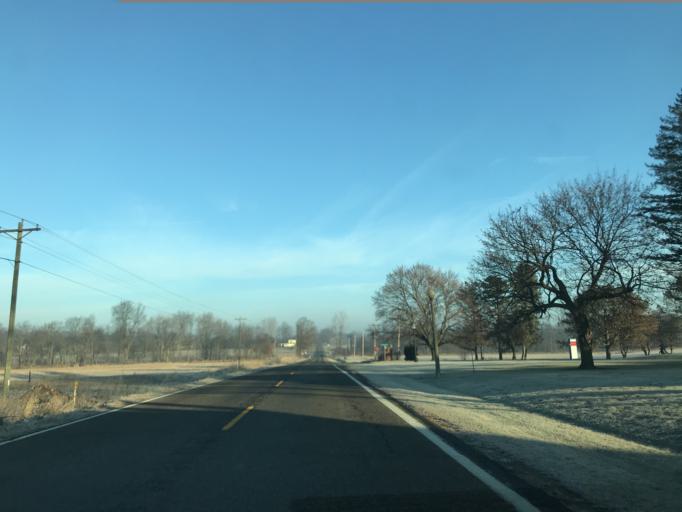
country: US
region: Michigan
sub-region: Eaton County
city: Eaton Rapids
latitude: 42.4780
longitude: -84.6009
